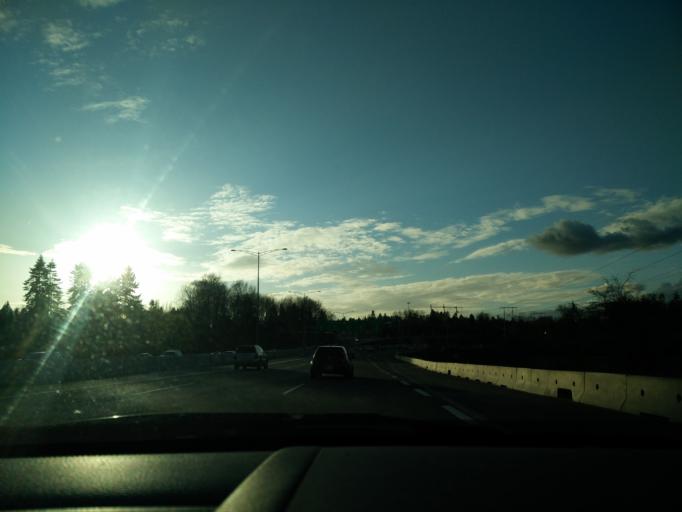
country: CA
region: British Columbia
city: Burnaby
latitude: 49.2416
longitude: -122.9611
